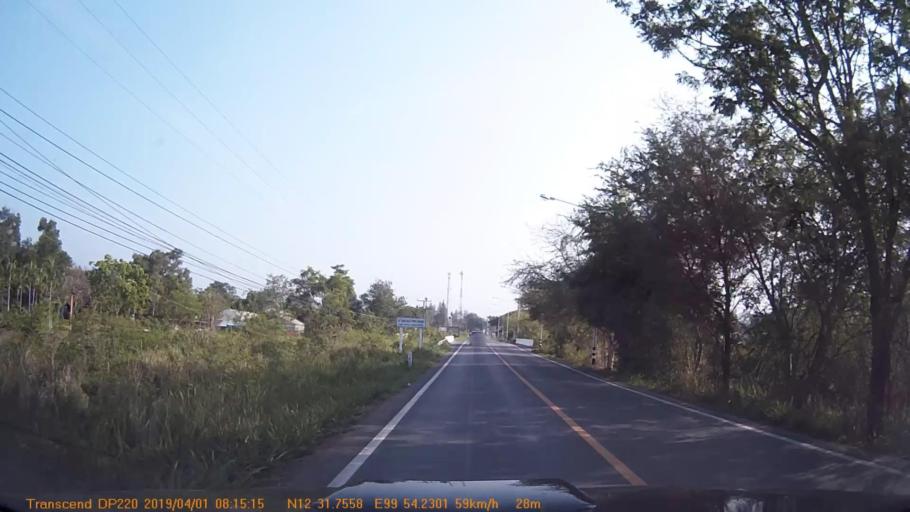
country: TH
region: Prachuap Khiri Khan
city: Hua Hin
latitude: 12.5295
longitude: 99.9039
